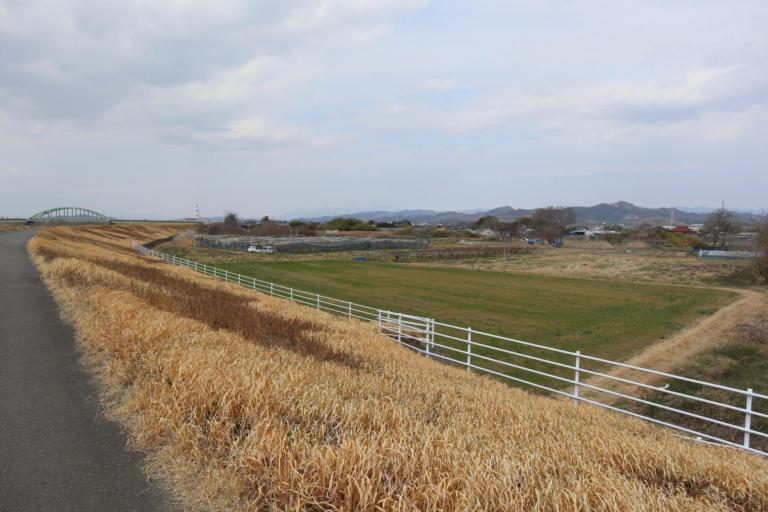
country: JP
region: Gunma
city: Tatebayashi
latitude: 36.2815
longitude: 139.5418
